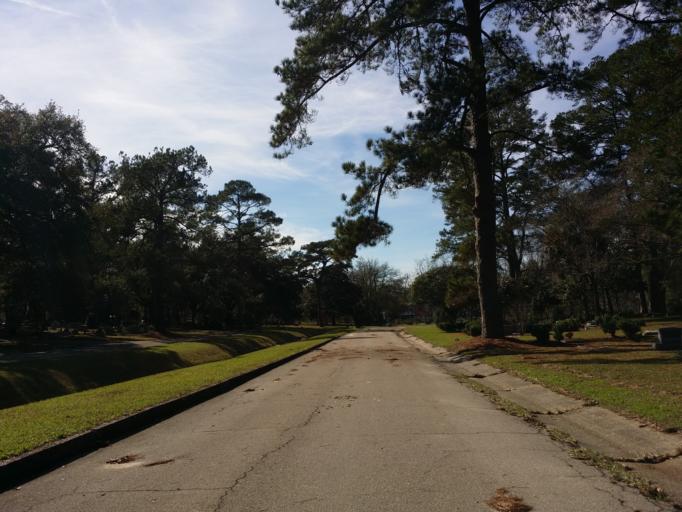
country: US
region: Florida
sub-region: Leon County
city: Tallahassee
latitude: 30.4521
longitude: -84.2863
